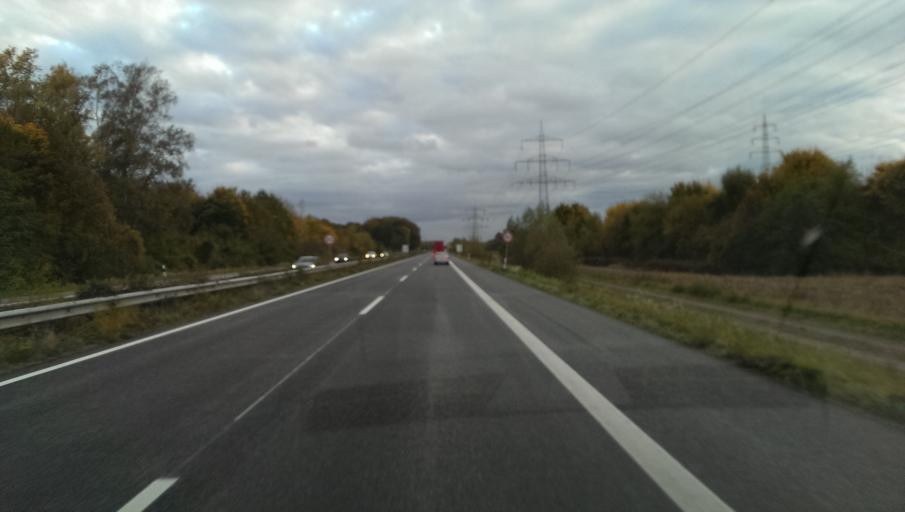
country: DE
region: Rheinland-Pfalz
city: Jockgrim
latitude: 49.0807
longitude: 8.2922
